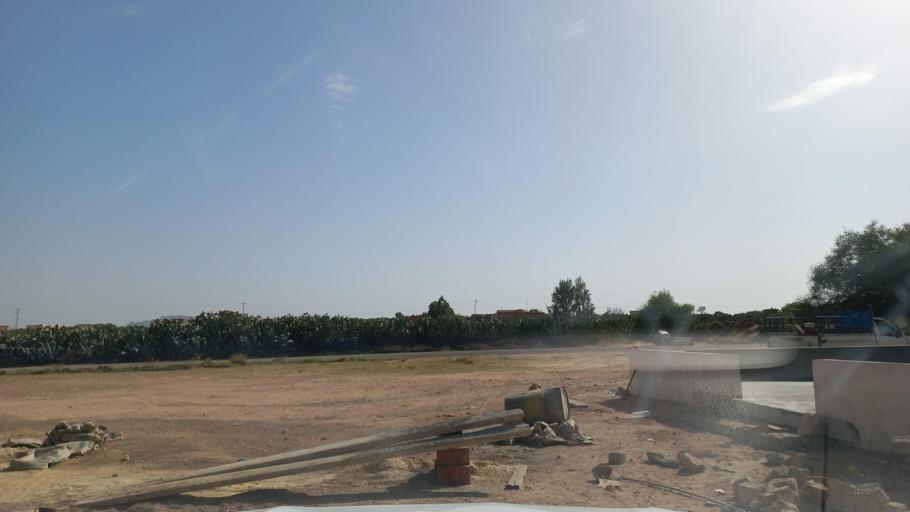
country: TN
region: Al Qasrayn
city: Kasserine
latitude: 35.2785
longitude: 8.9446
